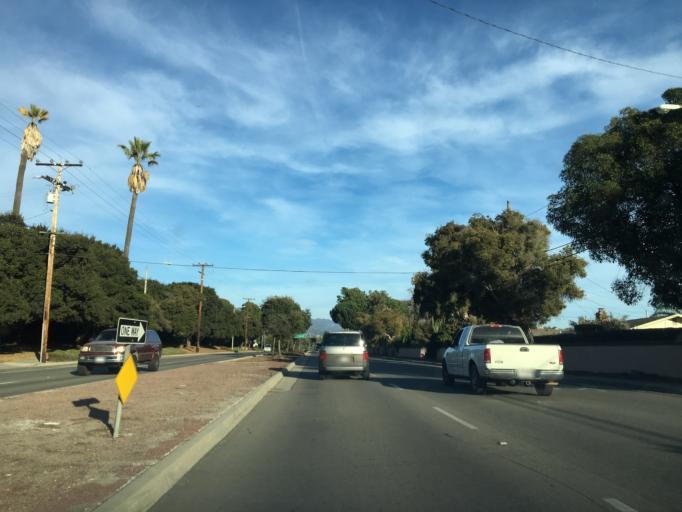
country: US
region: California
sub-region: Santa Barbara County
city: Goleta
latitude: 34.4349
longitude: -119.7985
